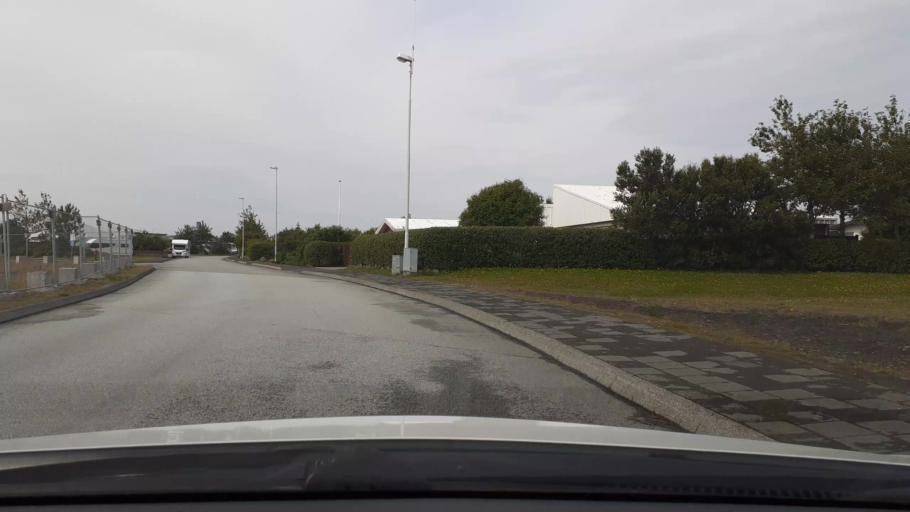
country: IS
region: Southern Peninsula
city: Reykjanesbaer
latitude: 63.9959
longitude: -22.5686
